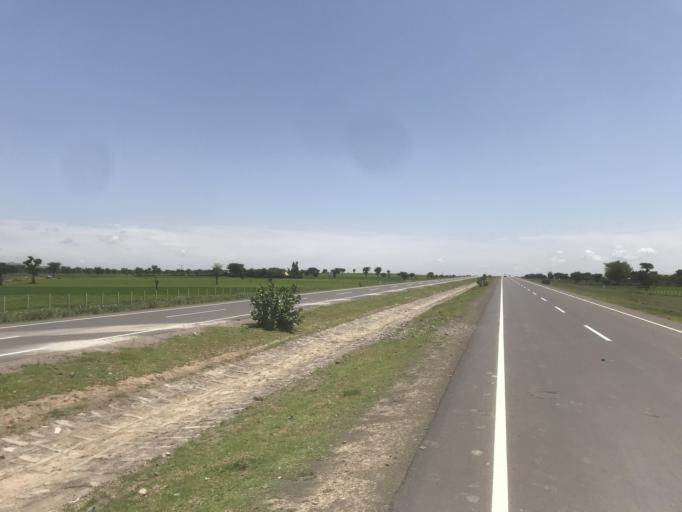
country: ET
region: Oromiya
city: Mojo
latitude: 8.3247
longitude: 38.9578
